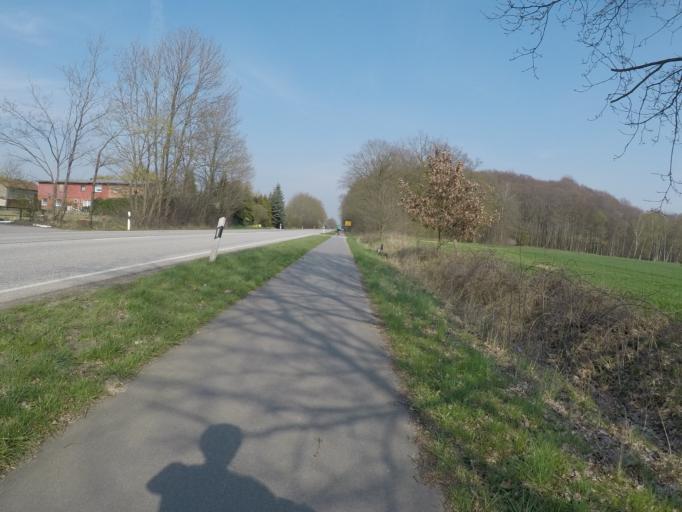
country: DE
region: Schleswig-Holstein
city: Seth
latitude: 53.8286
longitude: 10.2037
